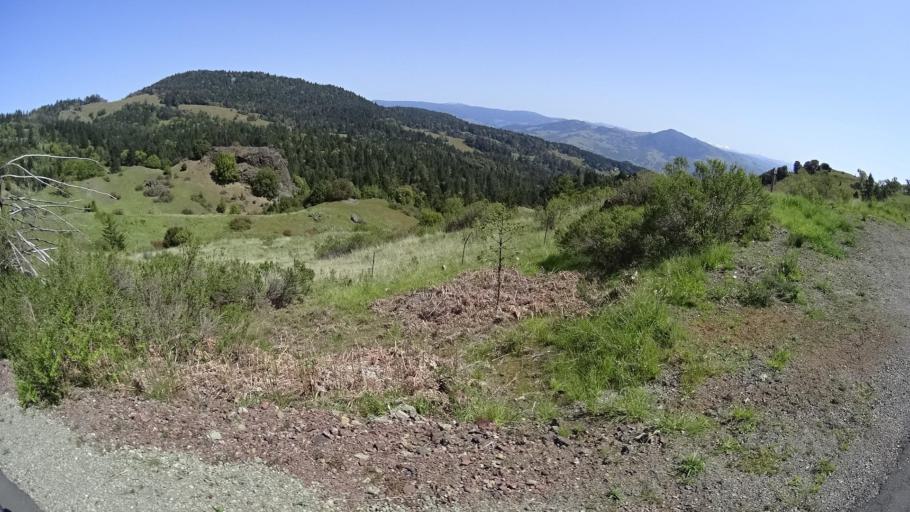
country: US
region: California
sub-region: Humboldt County
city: Redway
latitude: 40.1106
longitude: -123.6717
